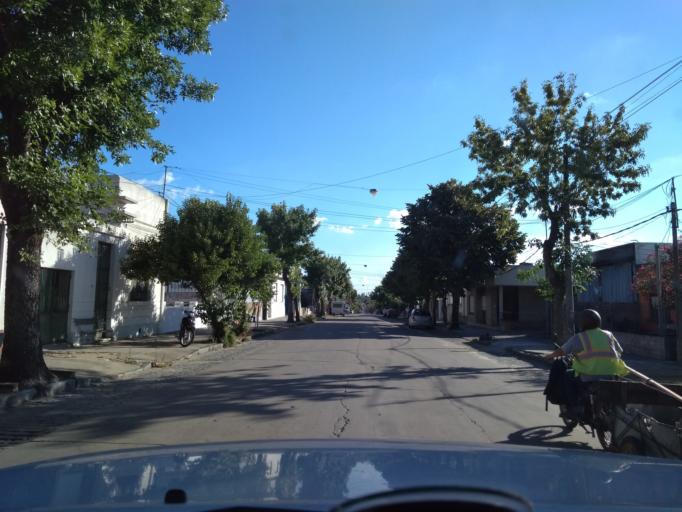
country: UY
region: Florida
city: Florida
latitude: -34.0940
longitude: -56.2211
